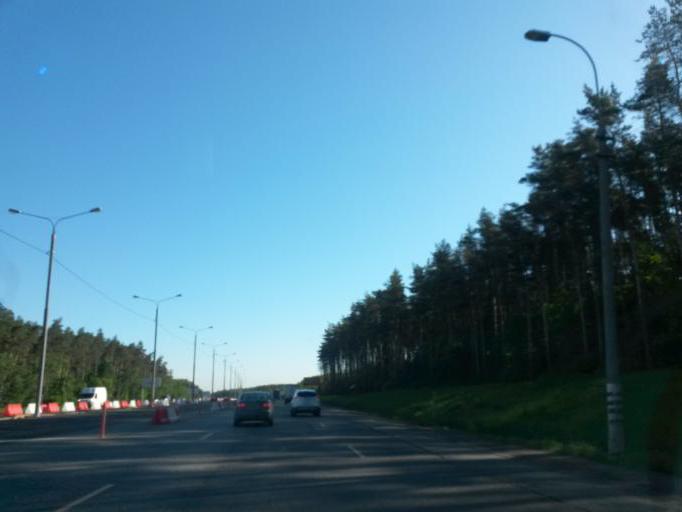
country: RU
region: Moskovskaya
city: Klimovsk
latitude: 55.3600
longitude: 37.5991
